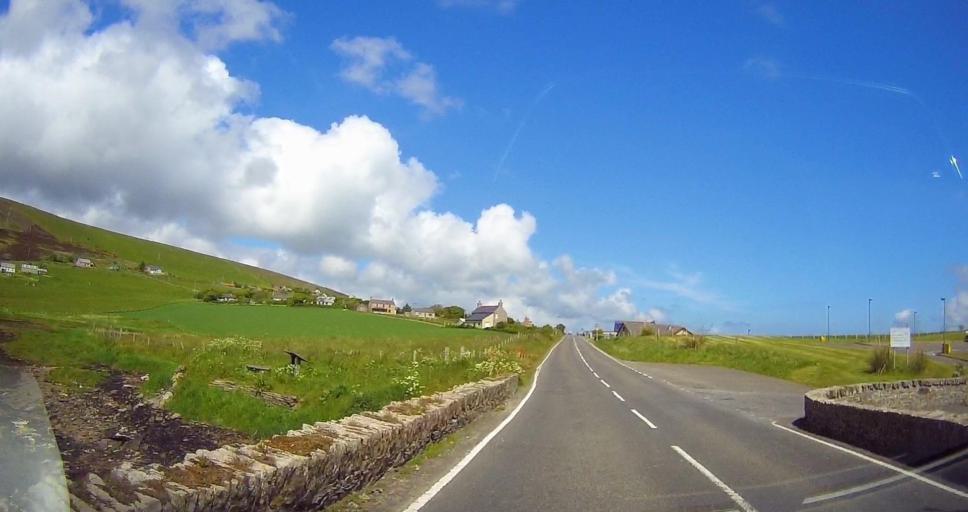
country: GB
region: Scotland
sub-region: Orkney Islands
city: Orkney
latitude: 59.0107
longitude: -3.1128
